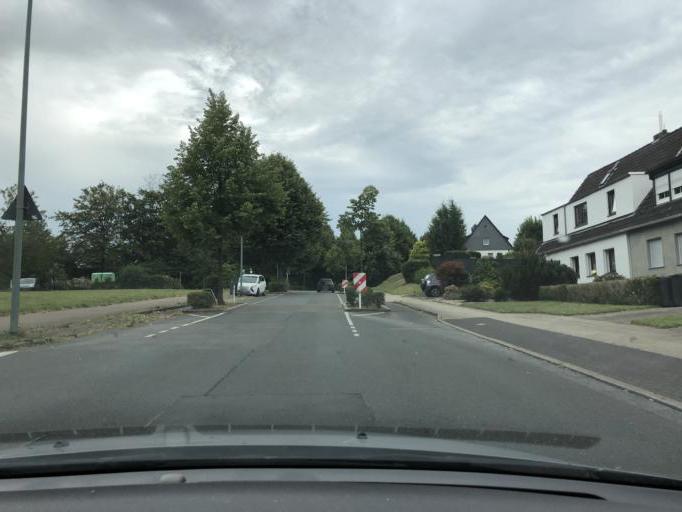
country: DE
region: North Rhine-Westphalia
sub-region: Regierungsbezirk Dusseldorf
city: Oberhausen
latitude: 51.4585
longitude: 6.9435
